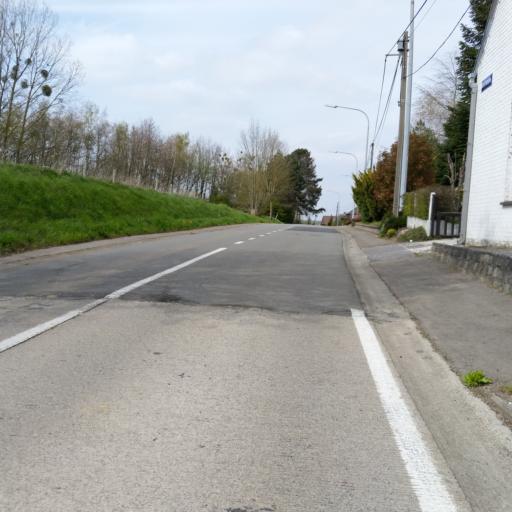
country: BE
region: Wallonia
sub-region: Province du Hainaut
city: Quevy-le-Petit
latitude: 50.3668
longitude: 3.9423
